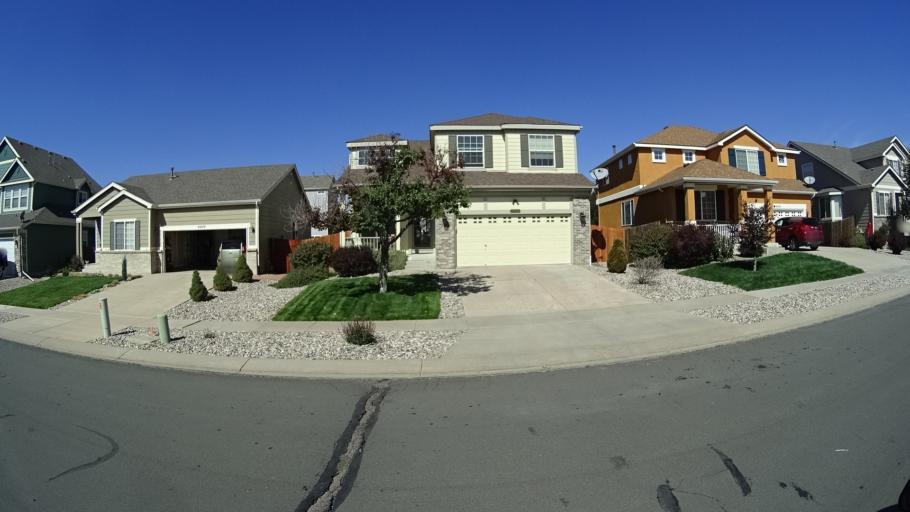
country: US
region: Colorado
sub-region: El Paso County
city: Cimarron Hills
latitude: 38.8968
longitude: -104.6953
